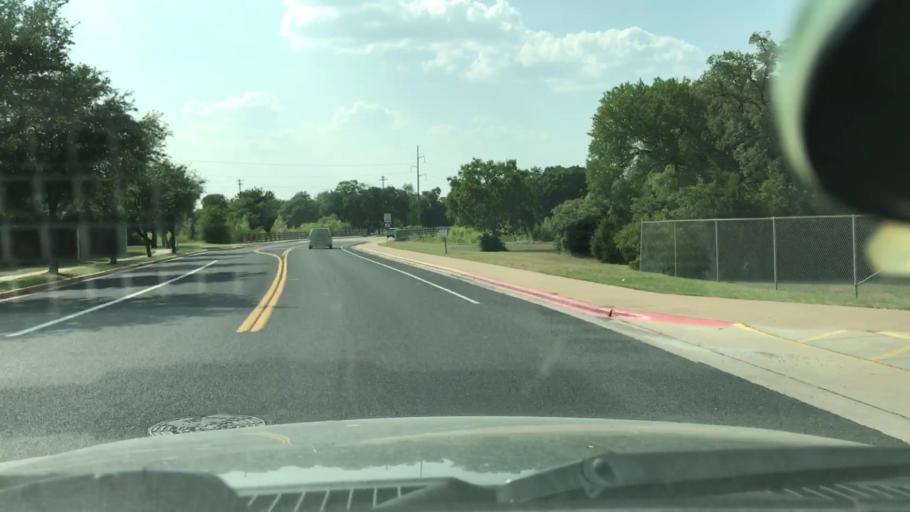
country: US
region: Texas
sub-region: Williamson County
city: Cedar Park
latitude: 30.5402
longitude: -97.8333
